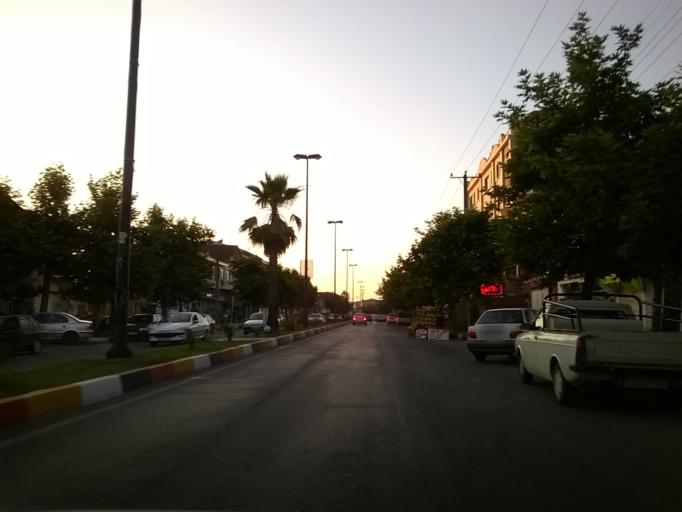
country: IR
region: Gilan
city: Astaneh-ye Ashrafiyeh
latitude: 37.2704
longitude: 49.9416
